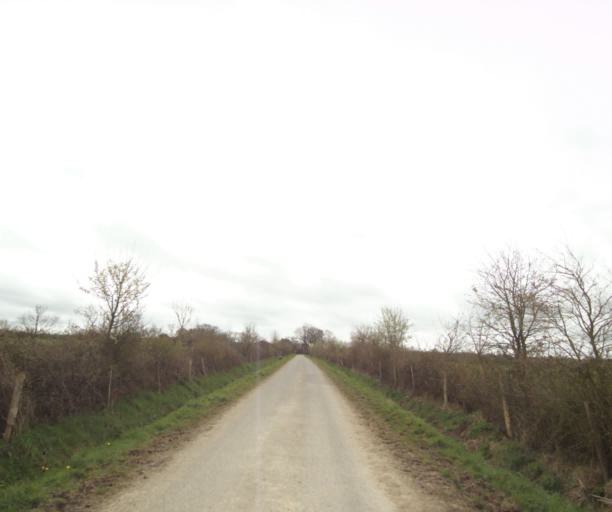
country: FR
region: Pays de la Loire
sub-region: Departement de la Loire-Atlantique
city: Bouvron
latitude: 47.4309
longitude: -1.8740
